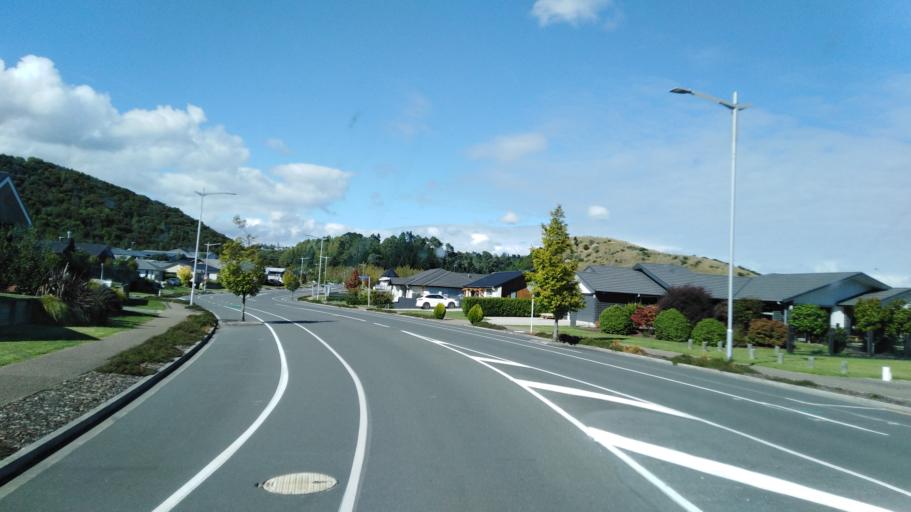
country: NZ
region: Bay of Plenty
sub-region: Tauranga City
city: Tauranga
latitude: -37.7543
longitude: 176.1040
